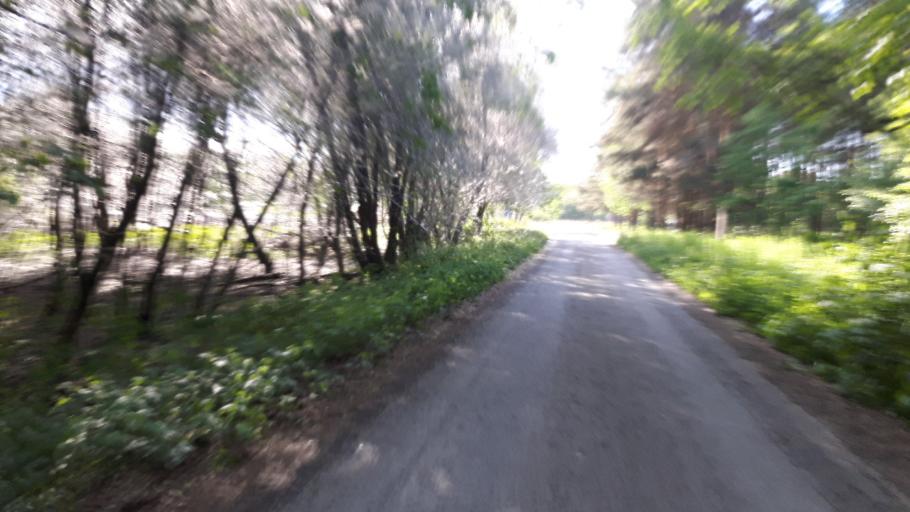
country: EE
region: Harju
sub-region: Tallinna linn
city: Kose
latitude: 59.4499
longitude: 24.9018
